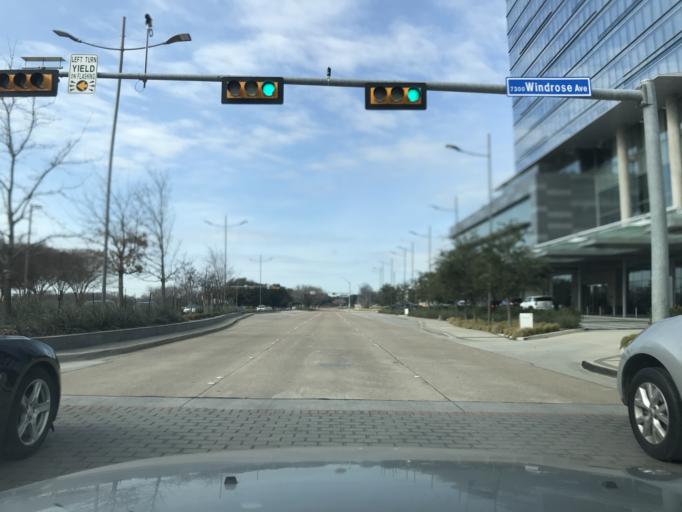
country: US
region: Texas
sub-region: Denton County
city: The Colony
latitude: 33.0781
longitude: -96.8267
